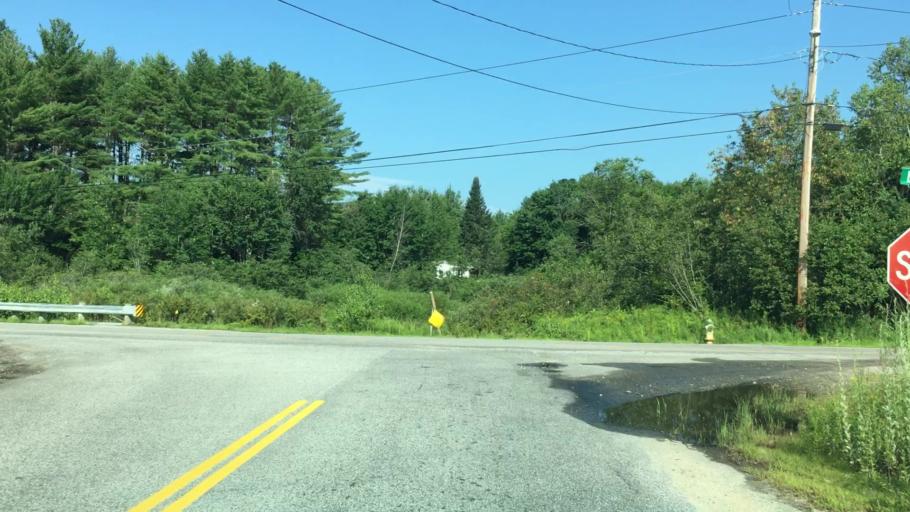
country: US
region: Maine
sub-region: Androscoggin County
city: Minot
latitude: 44.0451
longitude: -70.3298
